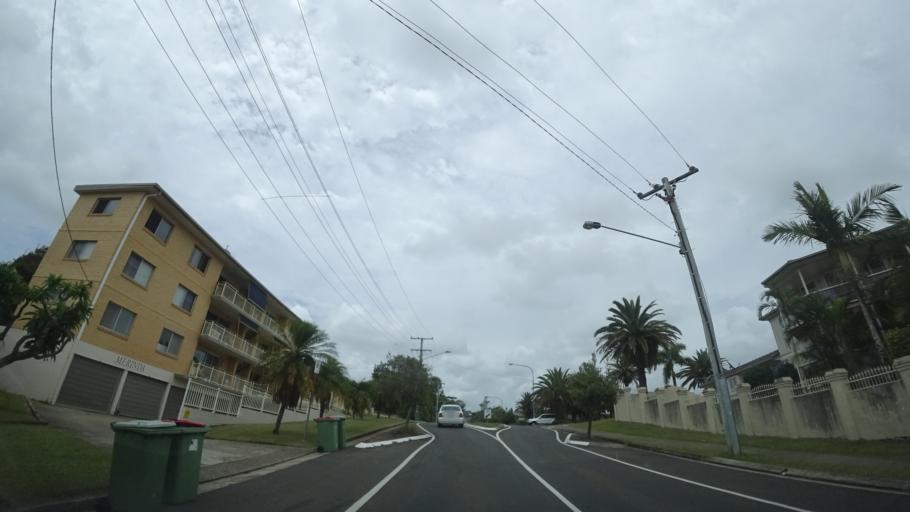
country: AU
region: Queensland
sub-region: Sunshine Coast
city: Mooloolaba
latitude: -26.6716
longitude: 153.1064
